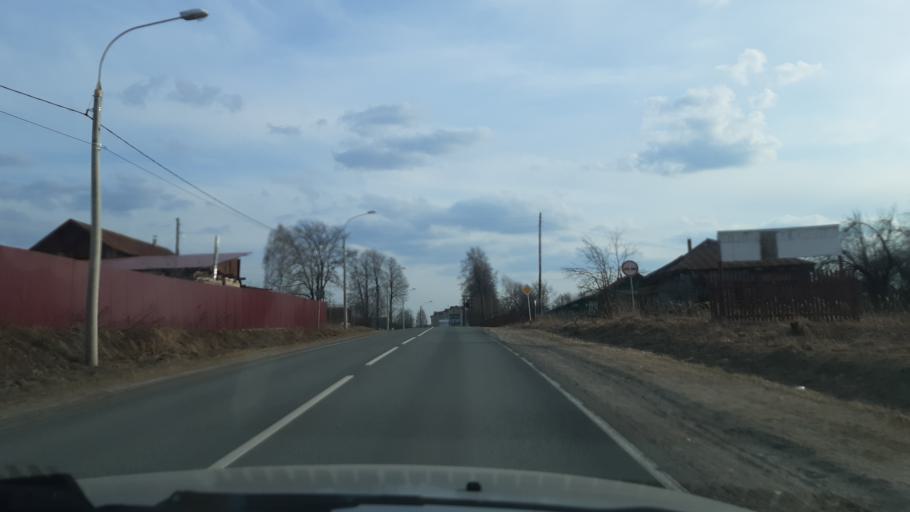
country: RU
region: Vladimir
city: Nikologory
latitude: 56.1520
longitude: 41.9956
